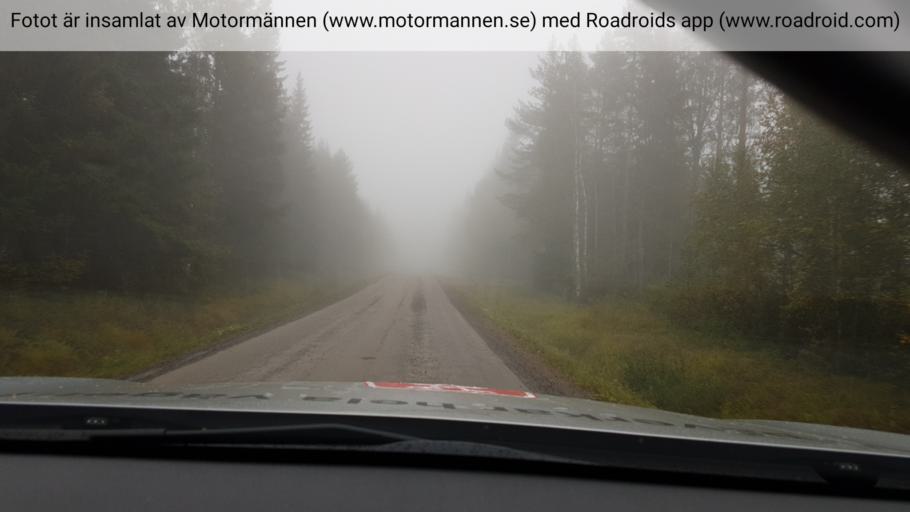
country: SE
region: Vaesterbotten
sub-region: Umea Kommun
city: Ersmark
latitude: 64.0928
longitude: 20.2362
